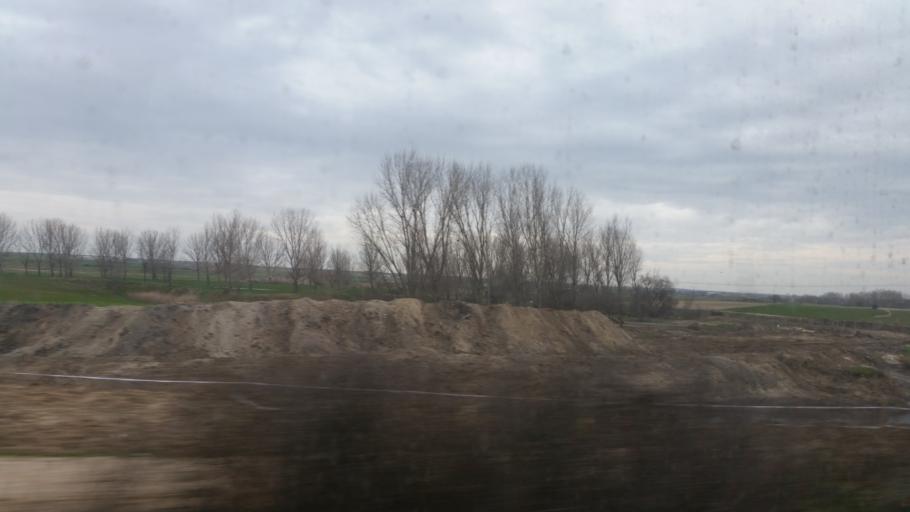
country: TR
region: Tekirdag
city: Corlu
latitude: 41.1954
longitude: 27.8146
